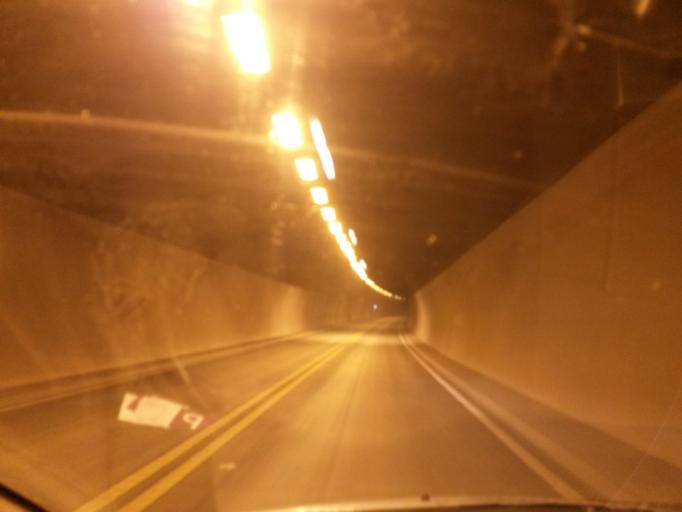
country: NO
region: Buskerud
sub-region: Drammen
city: Drammen
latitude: 59.7378
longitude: 10.1587
